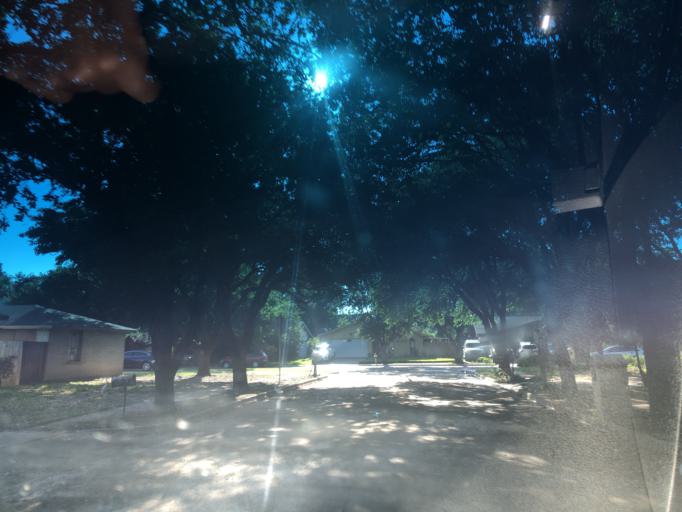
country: US
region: Texas
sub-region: Dallas County
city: Grand Prairie
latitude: 32.7051
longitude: -96.9994
